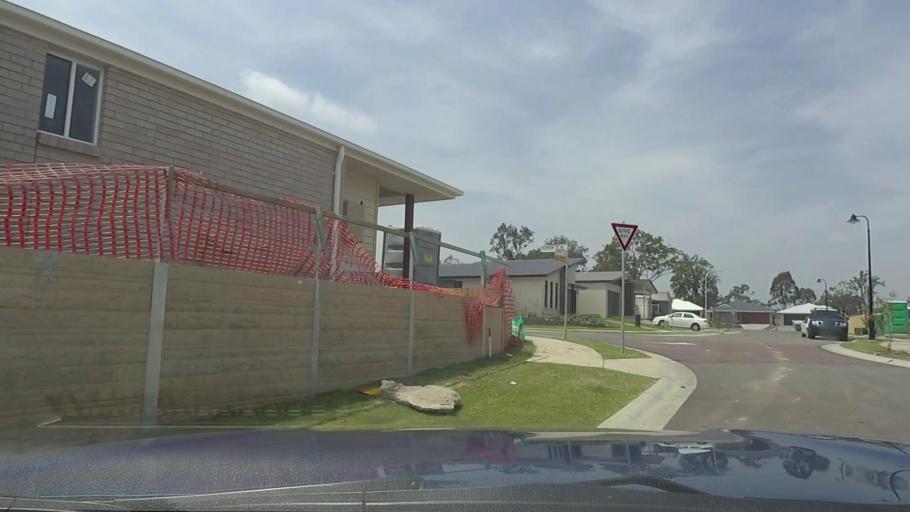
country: AU
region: Queensland
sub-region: Logan
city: Logan Reserve
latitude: -27.7036
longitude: 153.1038
